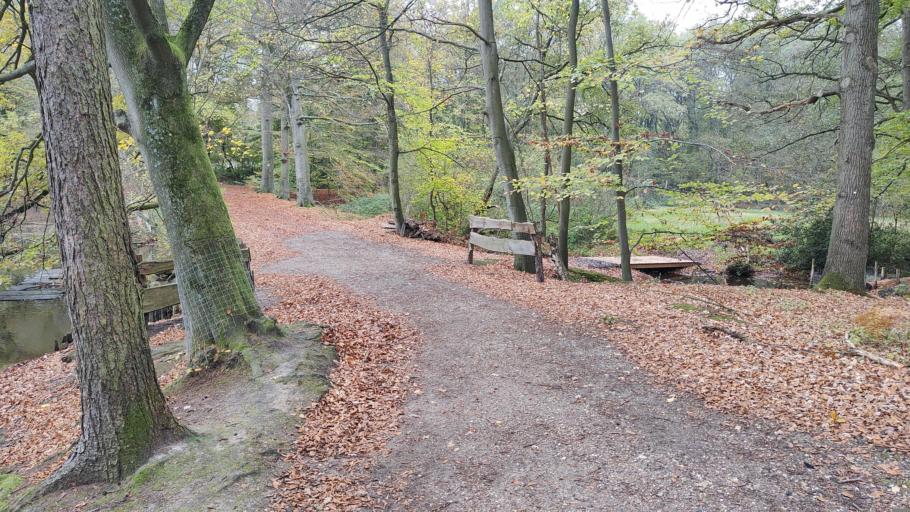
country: DE
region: North Rhine-Westphalia
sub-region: Regierungsbezirk Koln
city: Wassenberg
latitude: 51.1199
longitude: 6.1911
